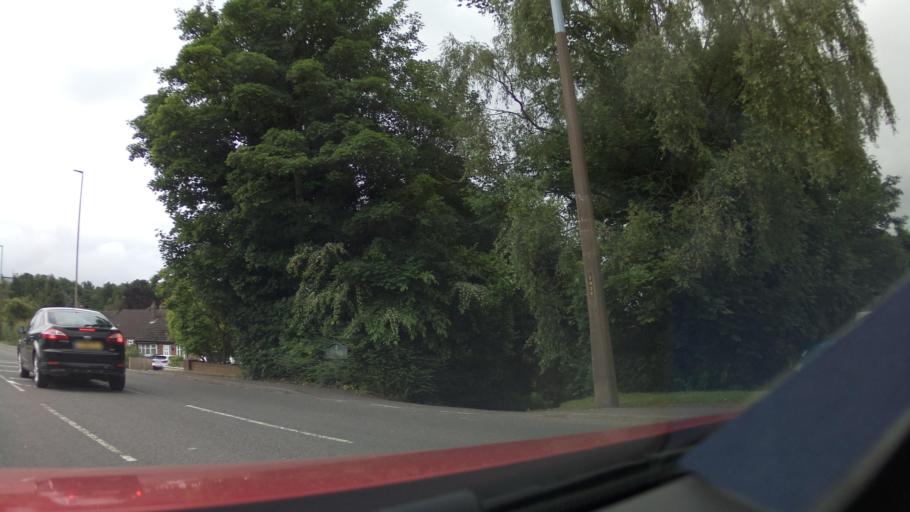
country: GB
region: England
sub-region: Derbyshire
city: Swadlincote
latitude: 52.7949
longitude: -1.5782
